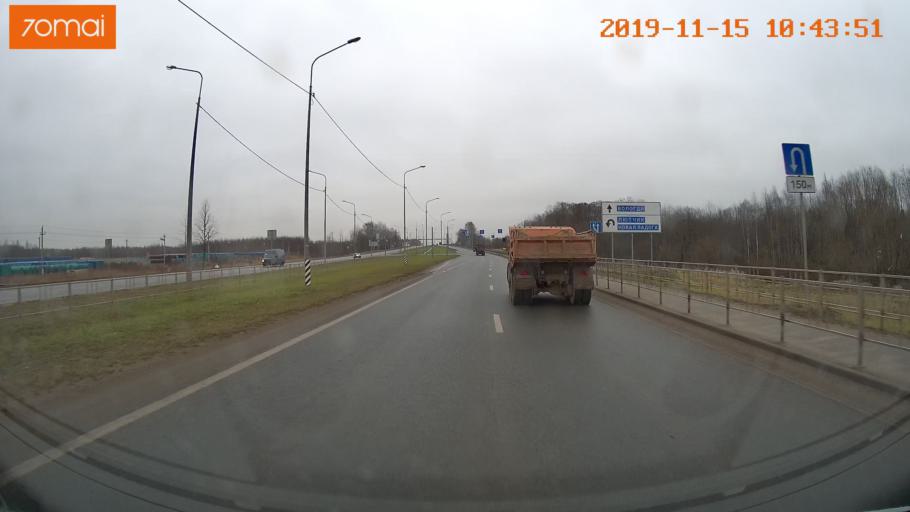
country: RU
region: Vologda
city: Sheksna
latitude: 59.2116
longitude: 38.5441
